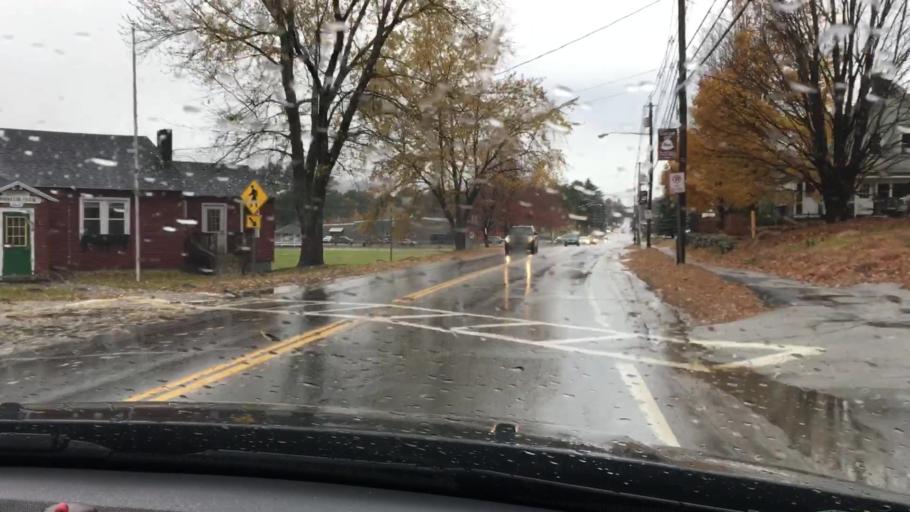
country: US
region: New Hampshire
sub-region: Grafton County
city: Ashland
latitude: 43.6959
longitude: -71.6363
